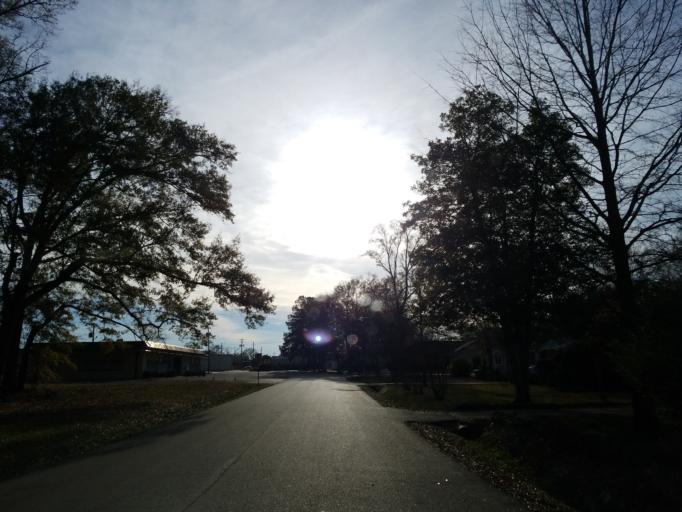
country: US
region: Mississippi
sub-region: Forrest County
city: Hattiesburg
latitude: 31.3184
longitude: -89.3021
